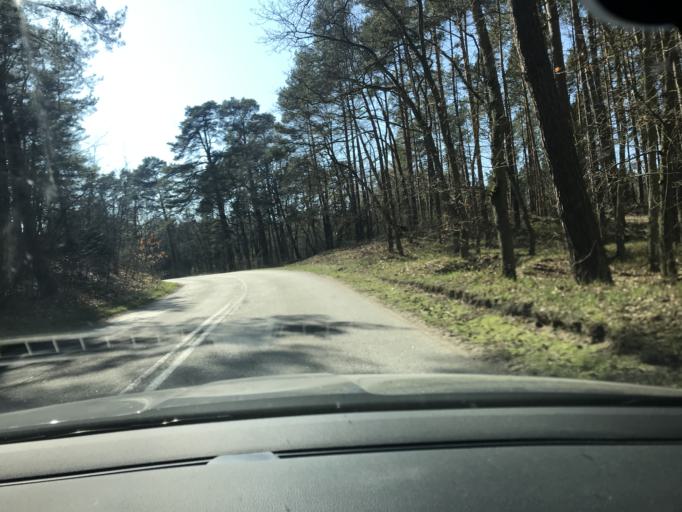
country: PL
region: Pomeranian Voivodeship
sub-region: Powiat nowodworski
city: Sztutowo
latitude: 54.3345
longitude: 19.1940
